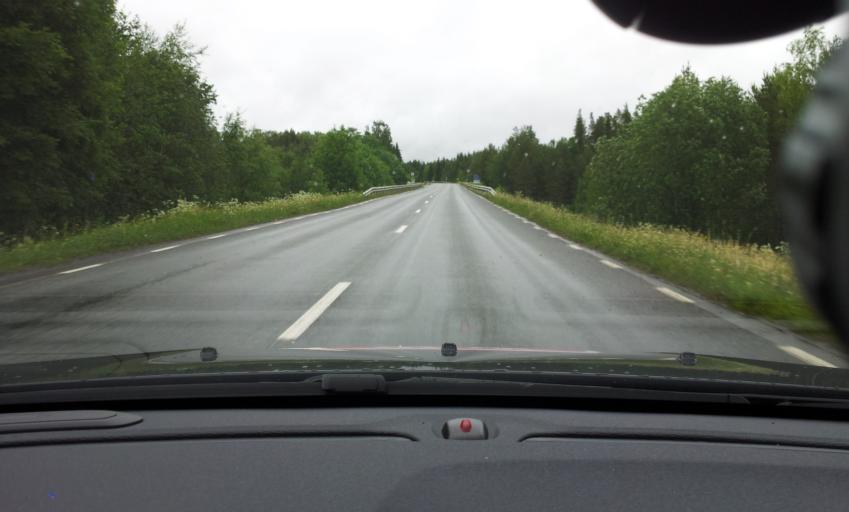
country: SE
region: Jaemtland
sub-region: Krokoms Kommun
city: Krokom
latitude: 63.3568
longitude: 14.4906
